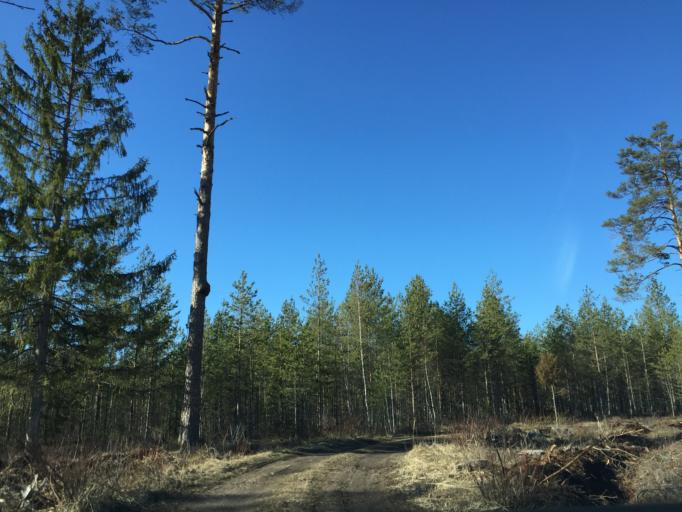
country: LV
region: Ropazu
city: Ropazi
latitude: 56.8909
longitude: 24.7069
